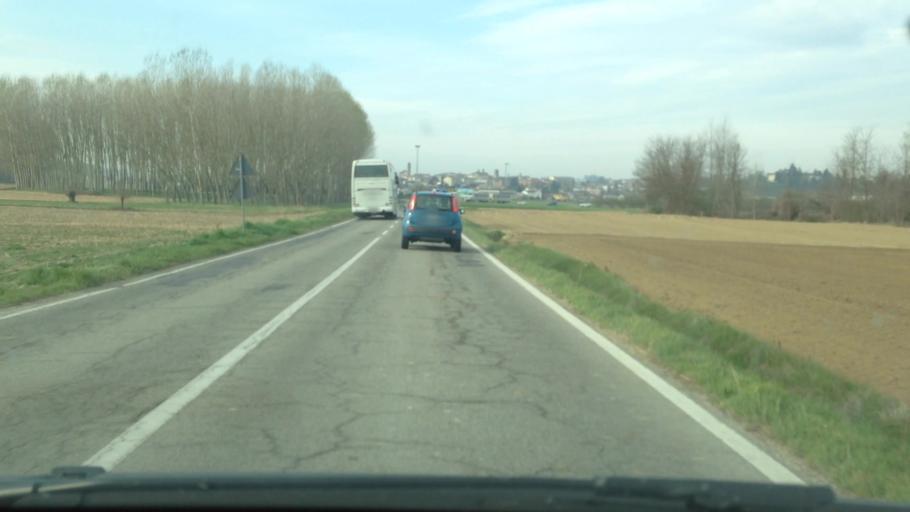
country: IT
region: Piedmont
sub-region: Provincia di Asti
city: San Damiano d'Asti
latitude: 44.8464
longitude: 8.0803
